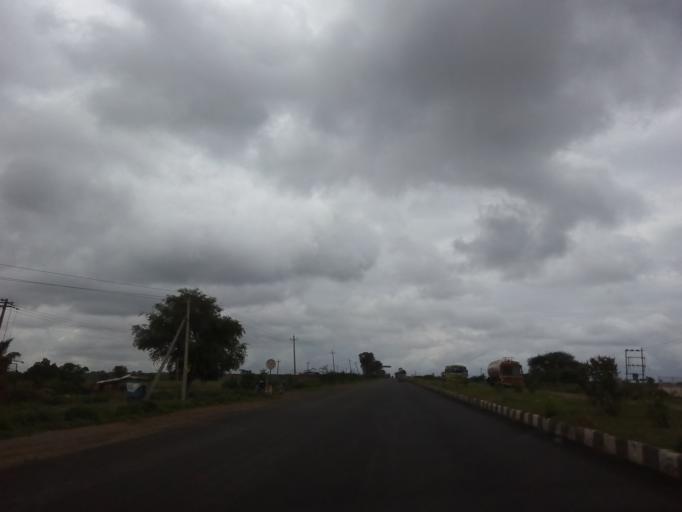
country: IN
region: Karnataka
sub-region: Haveri
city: Ranibennur
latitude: 14.6291
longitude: 75.5929
